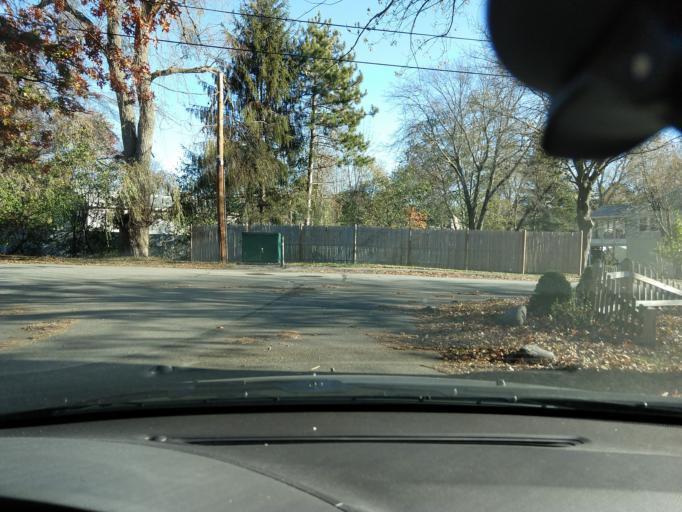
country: US
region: Massachusetts
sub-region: Middlesex County
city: Bedford
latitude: 42.4725
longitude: -71.2724
